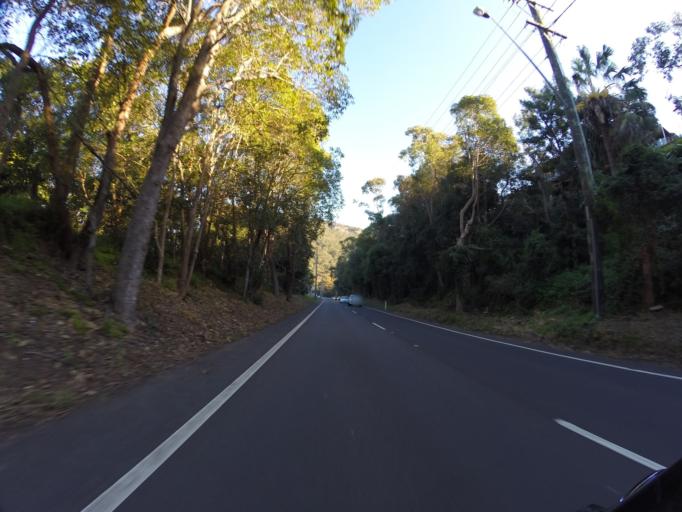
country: AU
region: New South Wales
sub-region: Wollongong
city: Helensburgh
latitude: -34.2281
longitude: 150.9833
